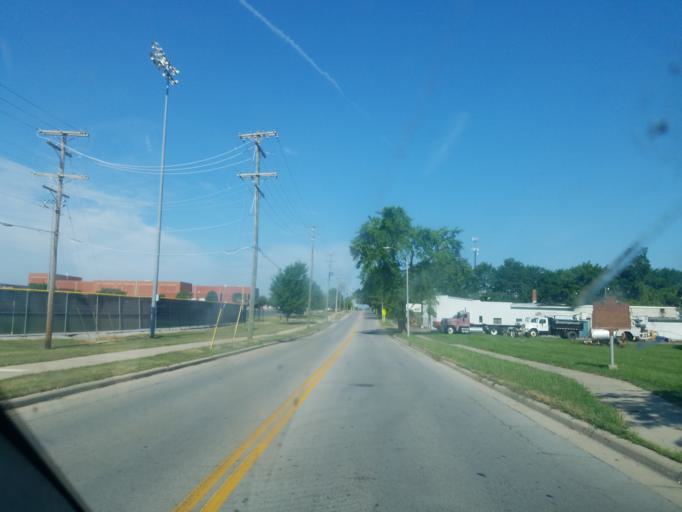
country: US
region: Ohio
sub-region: Allen County
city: Lima
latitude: 40.7426
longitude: -84.0929
